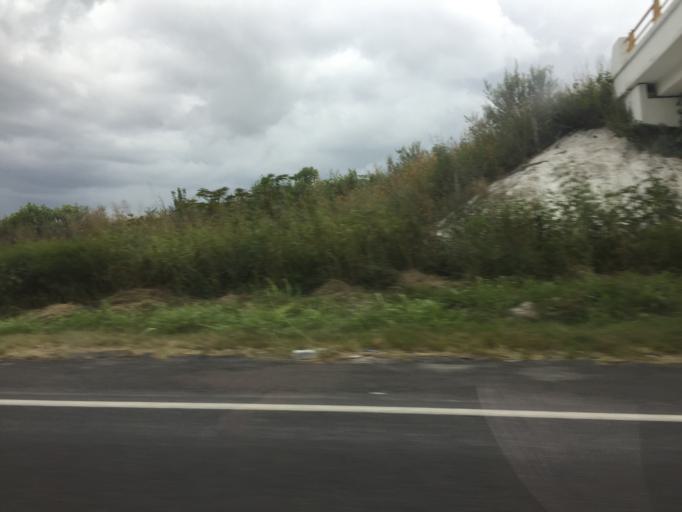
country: MX
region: Jalisco
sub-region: Zapotlanejo
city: La Mezquitera
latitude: 20.5778
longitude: -103.0905
